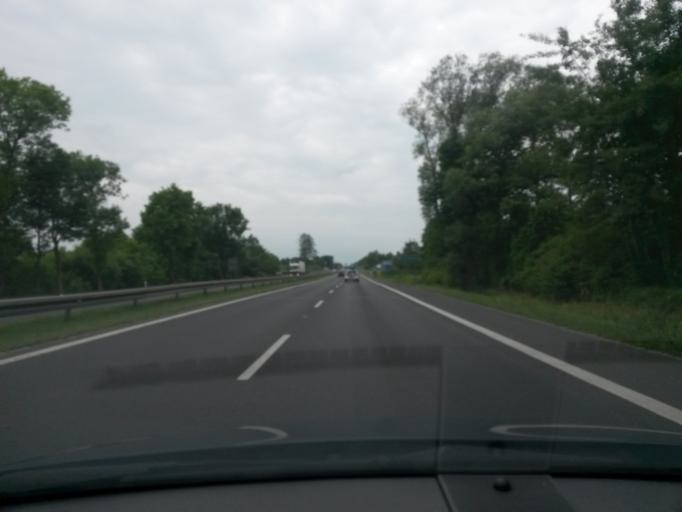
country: PL
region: Lodz Voivodeship
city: Zabia Wola
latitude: 52.0254
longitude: 20.6596
